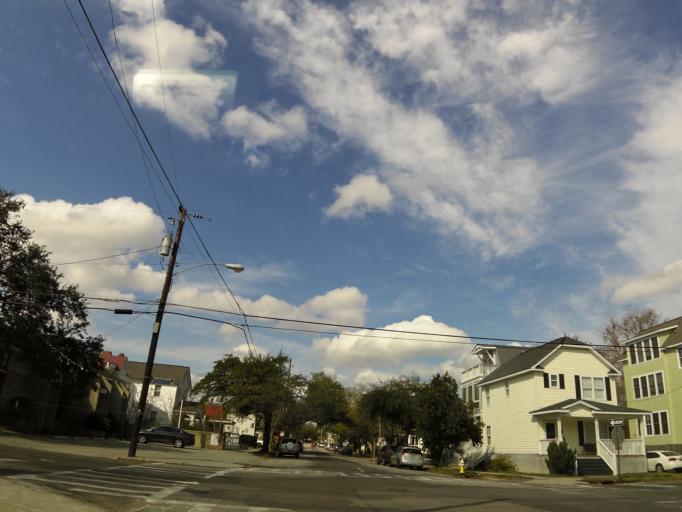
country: US
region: South Carolina
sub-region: Charleston County
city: Charleston
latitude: 32.7937
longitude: -79.9507
